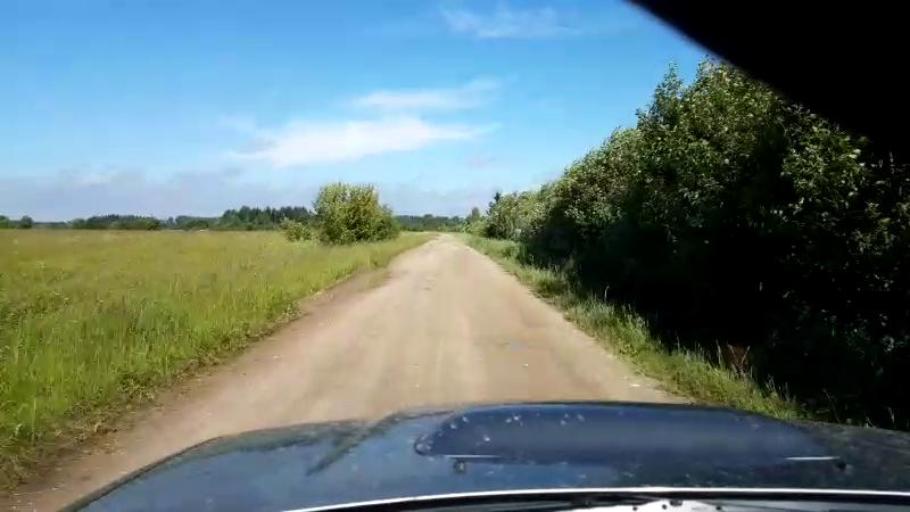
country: EE
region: Paernumaa
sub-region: Sindi linn
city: Sindi
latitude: 58.5045
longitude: 24.6974
